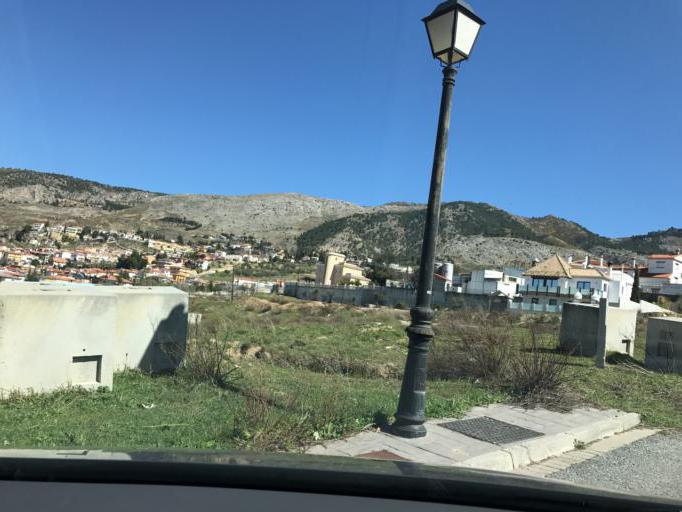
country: ES
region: Andalusia
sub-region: Provincia de Granada
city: Alfacar
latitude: 37.2341
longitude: -3.5638
